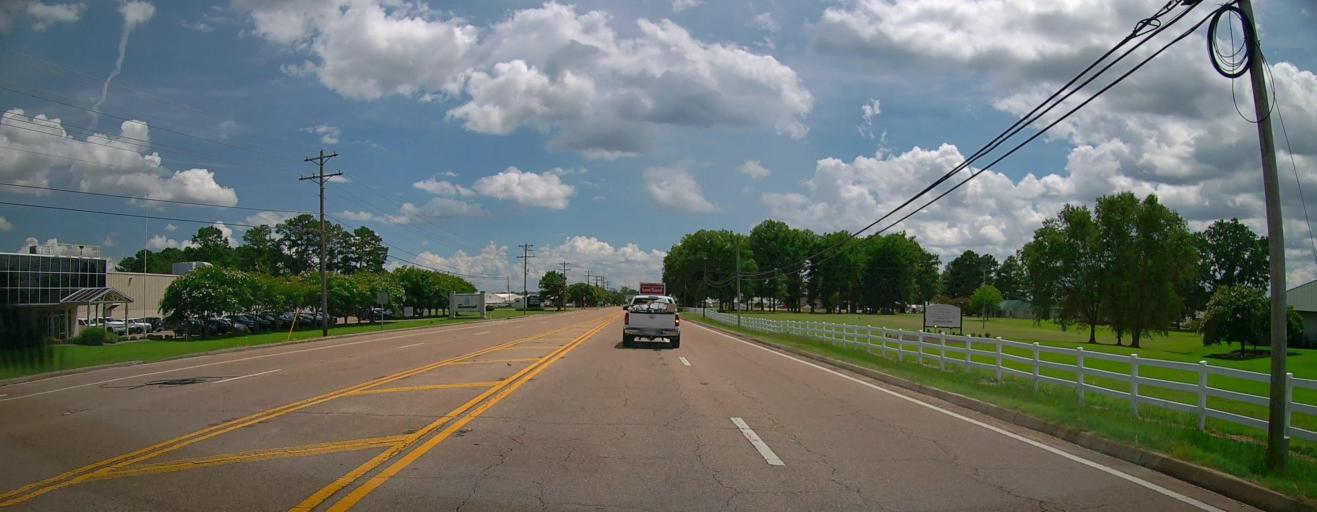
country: US
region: Mississippi
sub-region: Lee County
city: Verona
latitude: 34.1658
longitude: -88.7196
